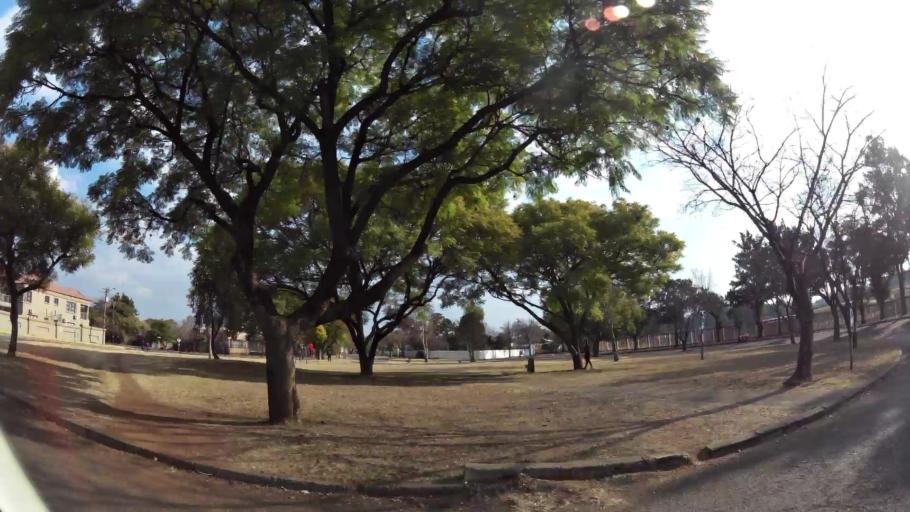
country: ZA
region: Gauteng
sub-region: Ekurhuleni Metropolitan Municipality
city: Germiston
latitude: -26.2293
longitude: 28.1768
